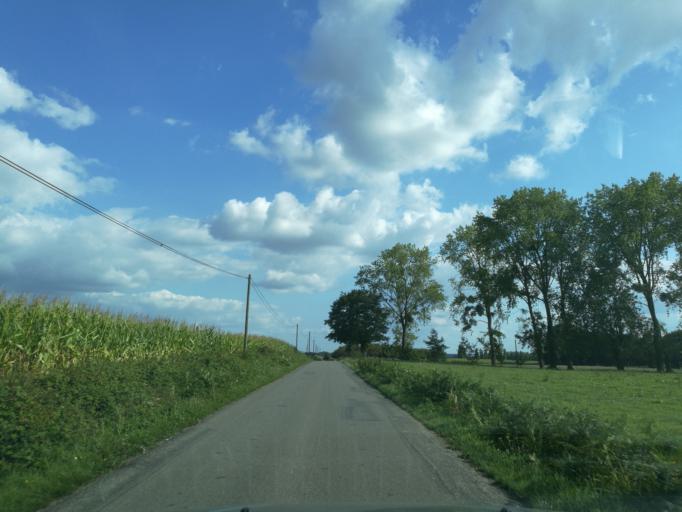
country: FR
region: Brittany
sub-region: Departement d'Ille-et-Vilaine
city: Bedee
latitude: 48.1951
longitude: -1.9652
